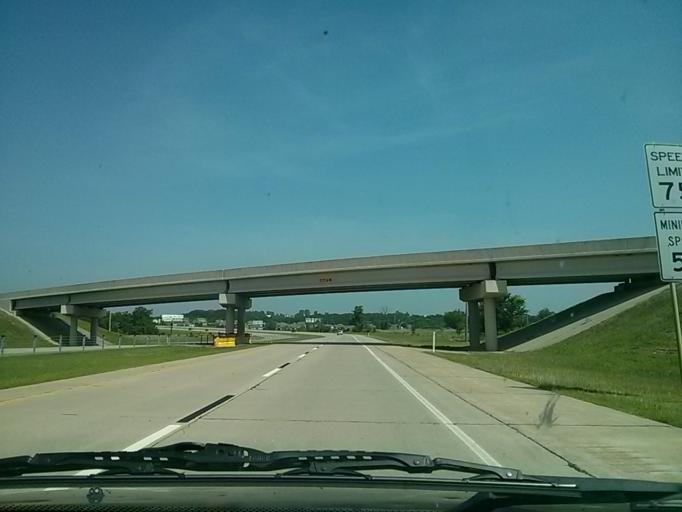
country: US
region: Oklahoma
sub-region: Creek County
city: Sapulpa
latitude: 36.0241
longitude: -96.0752
